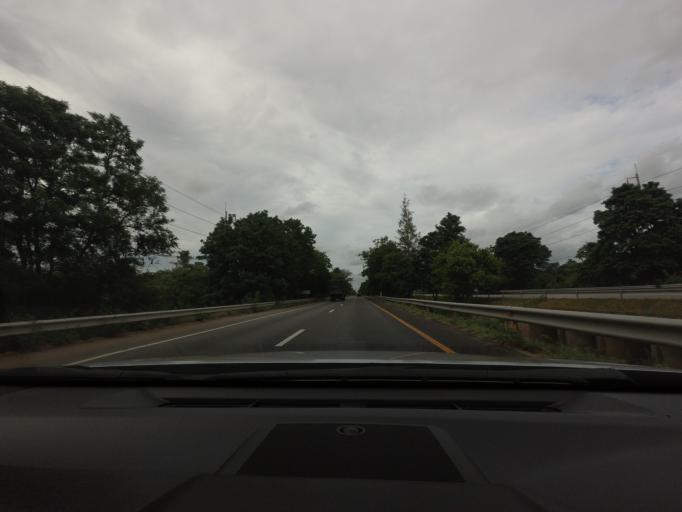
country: TH
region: Prachuap Khiri Khan
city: Hua Hin
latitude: 12.6373
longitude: 99.8602
